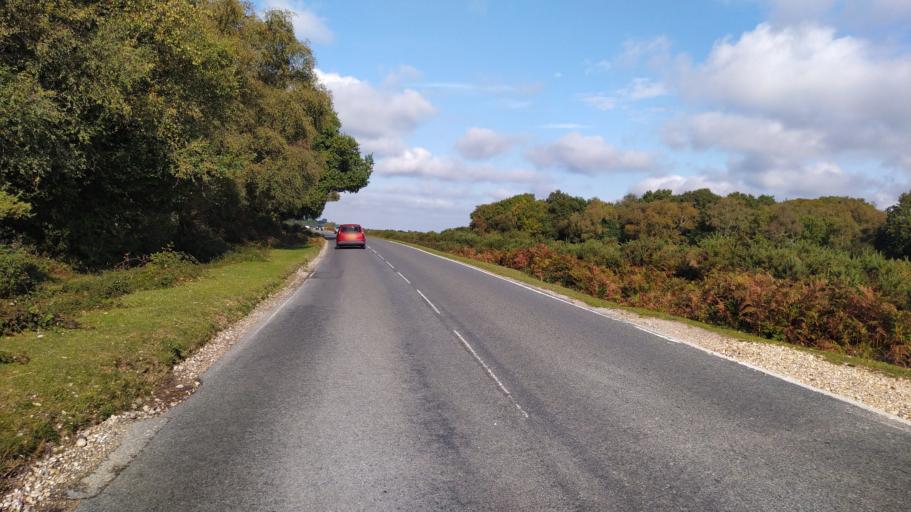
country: GB
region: England
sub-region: Hampshire
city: Bransgore
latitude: 50.8432
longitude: -1.7219
